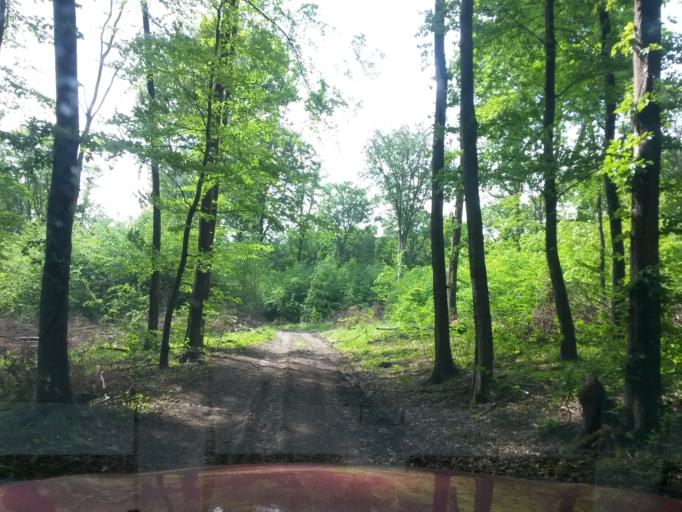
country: SK
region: Kosicky
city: Kosice
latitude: 48.7543
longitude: 21.2279
